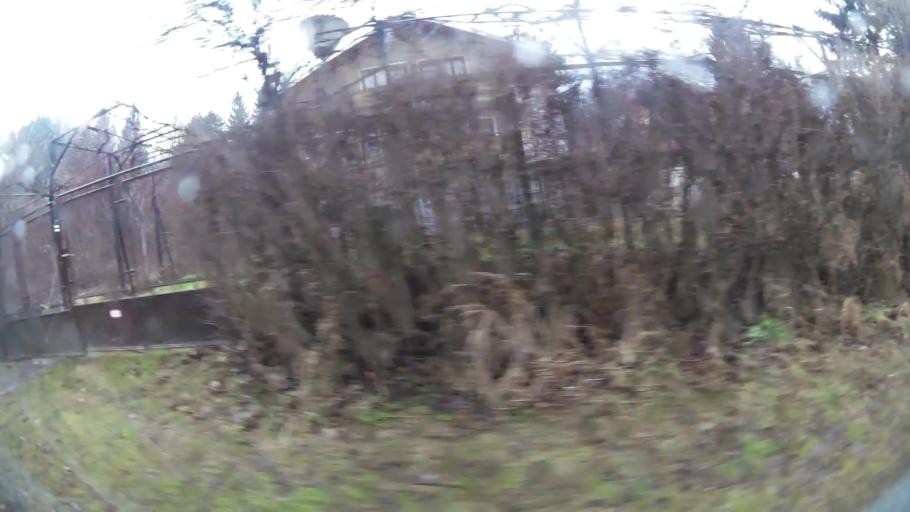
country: BG
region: Sofia-Capital
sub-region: Stolichna Obshtina
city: Sofia
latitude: 42.5997
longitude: 23.3945
